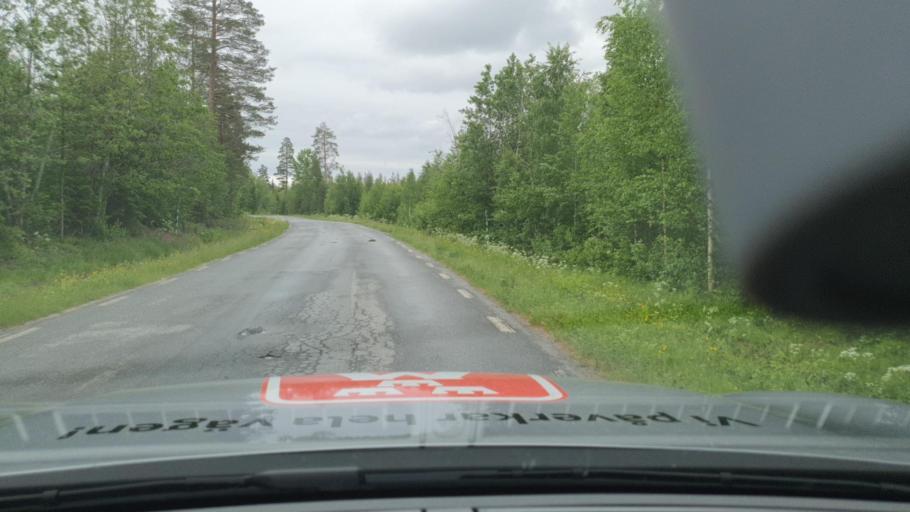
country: SE
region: Norrbotten
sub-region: Lulea Kommun
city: Ranea
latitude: 65.8309
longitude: 22.3154
